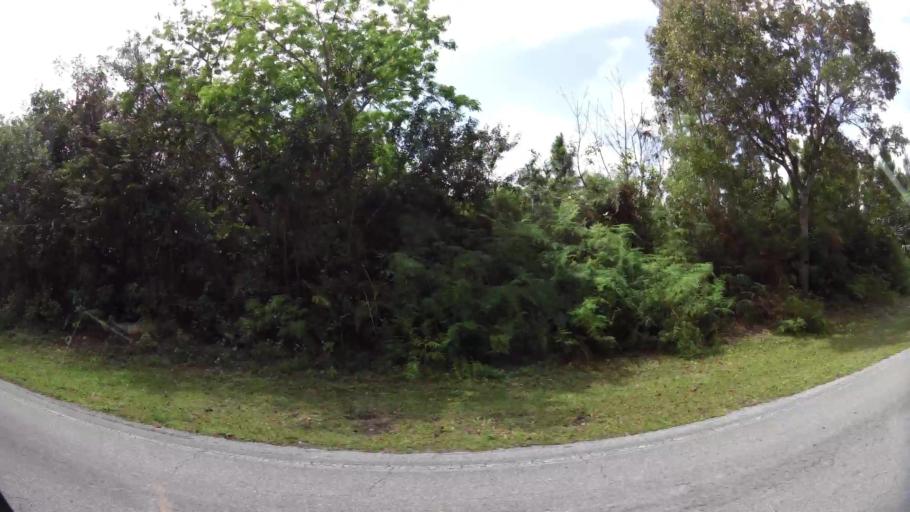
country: BS
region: Freeport
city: Lucaya
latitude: 26.5214
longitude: -78.6504
